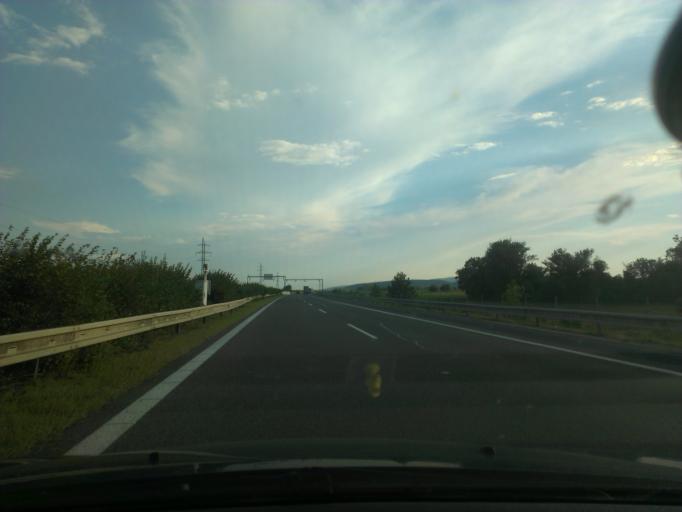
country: SK
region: Trenciansky
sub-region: Okres Trencin
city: Trencin
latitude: 48.8420
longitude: 17.9408
